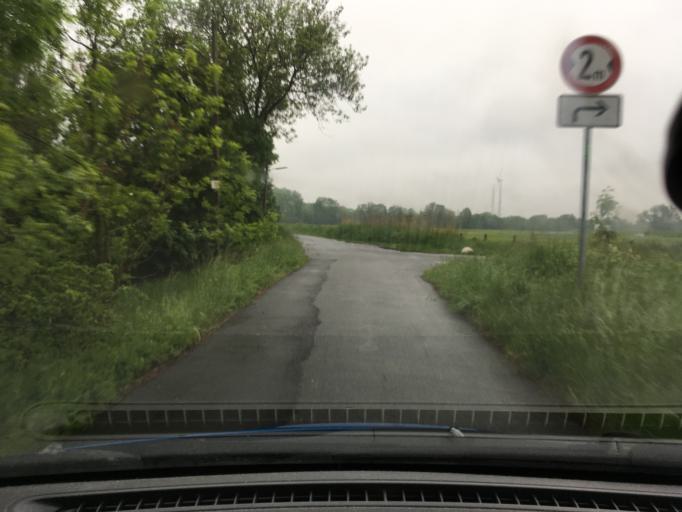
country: DE
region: Hamburg
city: Rothenburgsort
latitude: 53.4959
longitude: 10.0426
